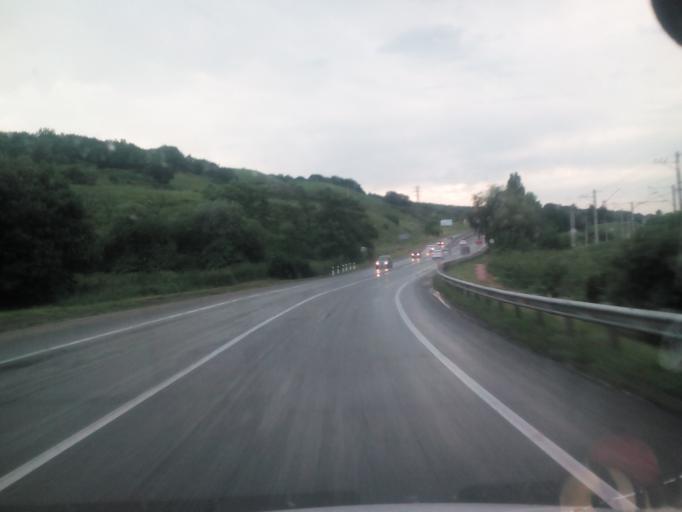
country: RU
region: Stavropol'skiy
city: Yasnaya Polyana
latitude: 44.0046
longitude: 42.7951
